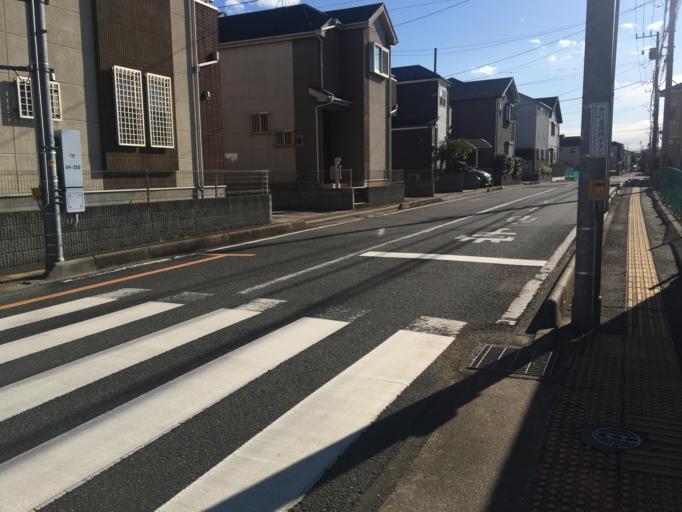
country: JP
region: Saitama
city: Shiki
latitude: 35.8240
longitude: 139.5644
